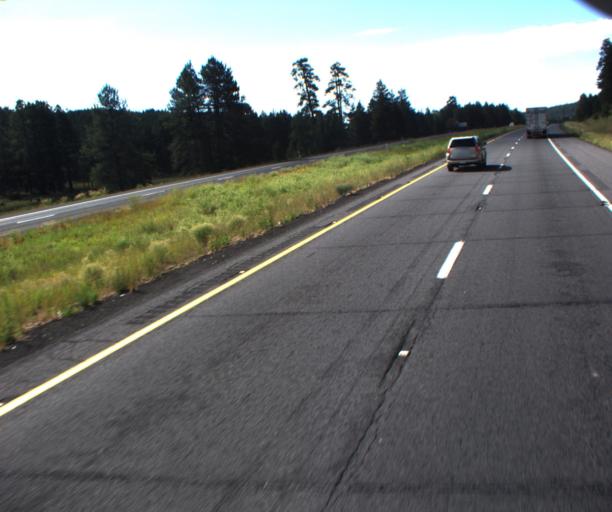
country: US
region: Arizona
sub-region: Coconino County
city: Mountainaire
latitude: 34.9675
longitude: -111.6827
